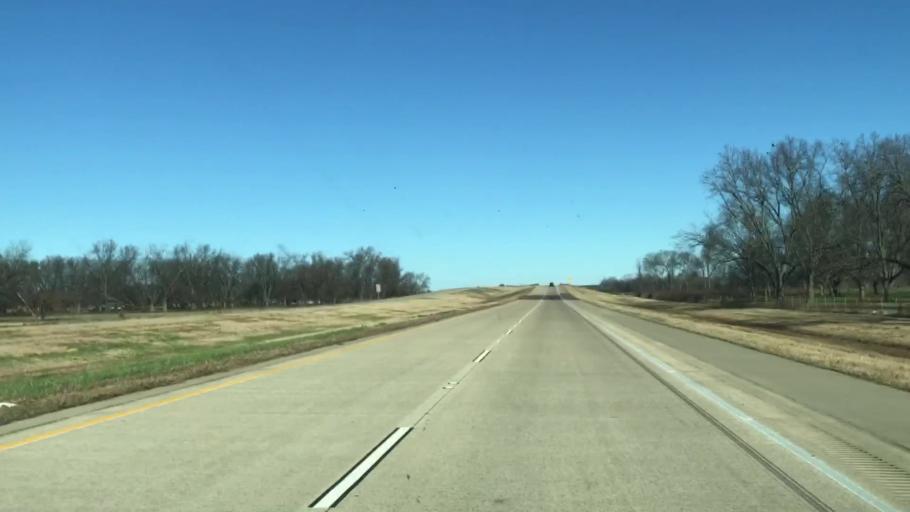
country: US
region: Louisiana
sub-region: Caddo Parish
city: Oil City
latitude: 32.7413
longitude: -93.8778
